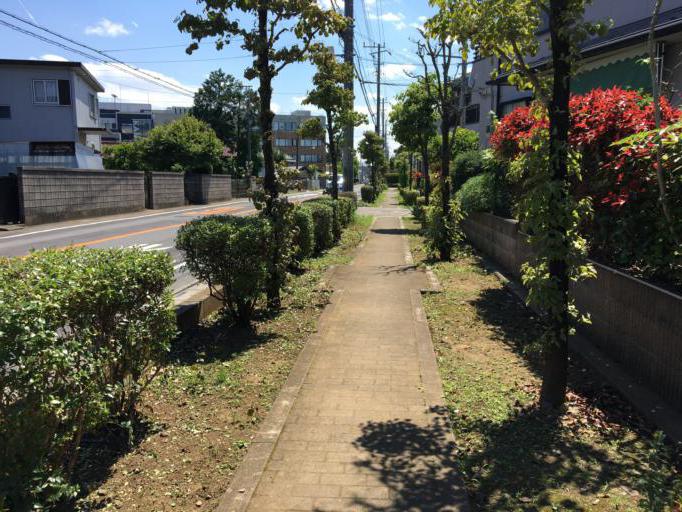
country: JP
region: Saitama
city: Sakado
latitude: 35.9512
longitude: 139.3871
